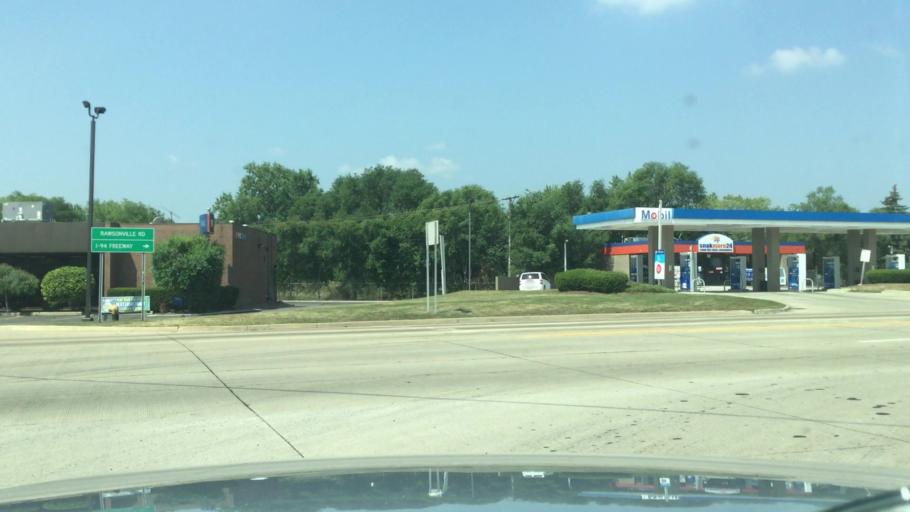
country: US
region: Michigan
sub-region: Wayne County
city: Belleville
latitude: 42.2155
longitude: -83.5440
